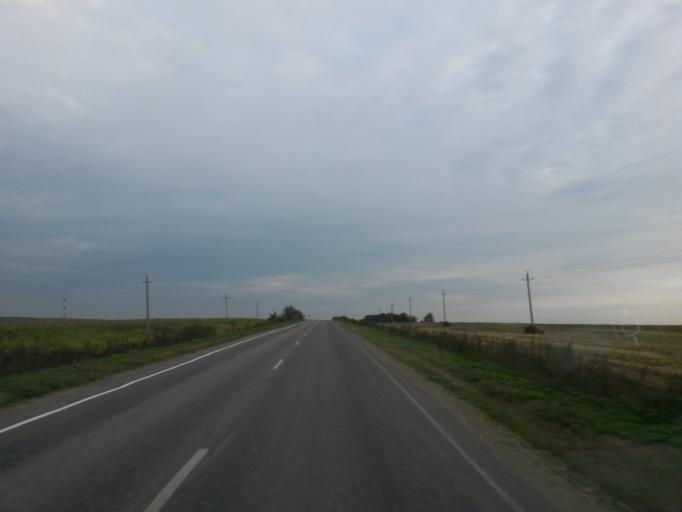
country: RU
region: Moskovskaya
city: Barybino
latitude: 55.2064
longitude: 37.7886
